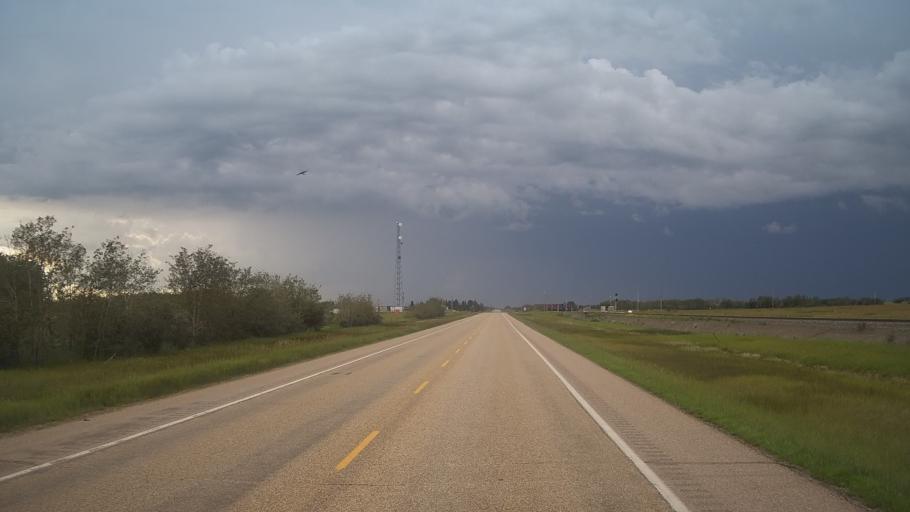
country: CA
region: Alberta
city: Tofield
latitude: 53.2677
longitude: -112.3628
